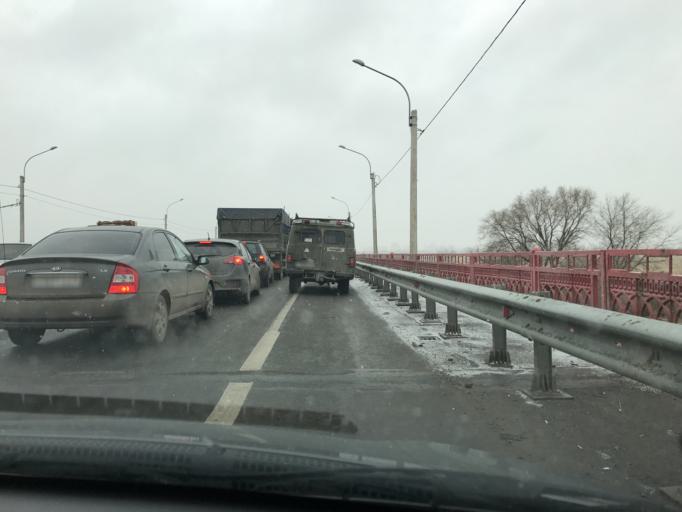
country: RU
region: Rostov
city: Bataysk
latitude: 47.1816
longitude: 39.7393
